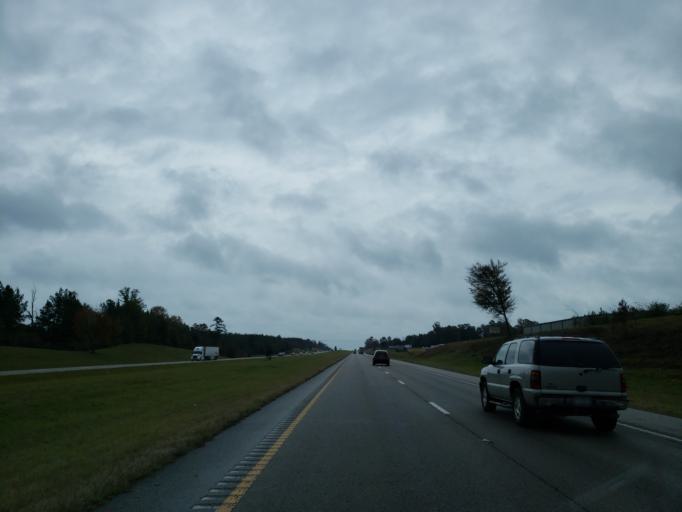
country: US
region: Mississippi
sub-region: Jones County
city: Ellisville
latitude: 31.5324
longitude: -89.2772
